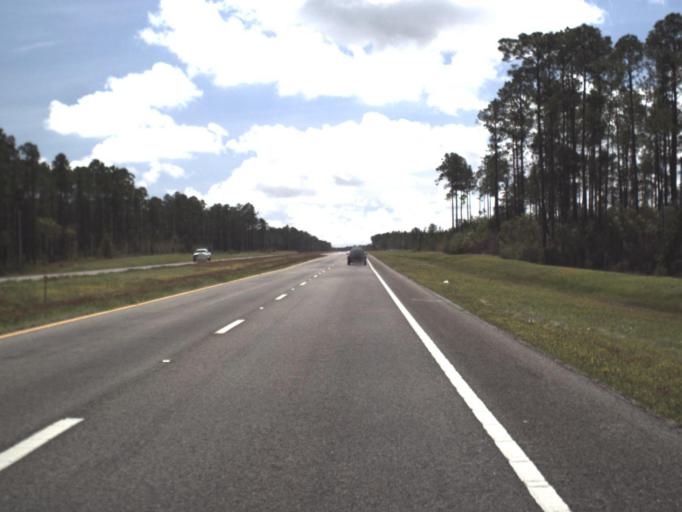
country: US
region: Florida
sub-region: Bay County
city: Laguna Beach
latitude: 30.4096
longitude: -85.8698
